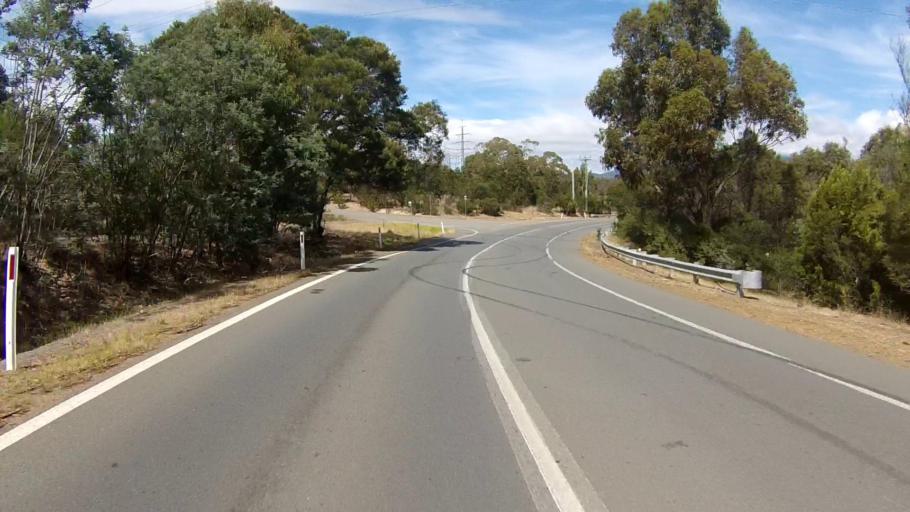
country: AU
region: Tasmania
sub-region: Clarence
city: Lindisfarne
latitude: -42.8228
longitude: 147.3495
